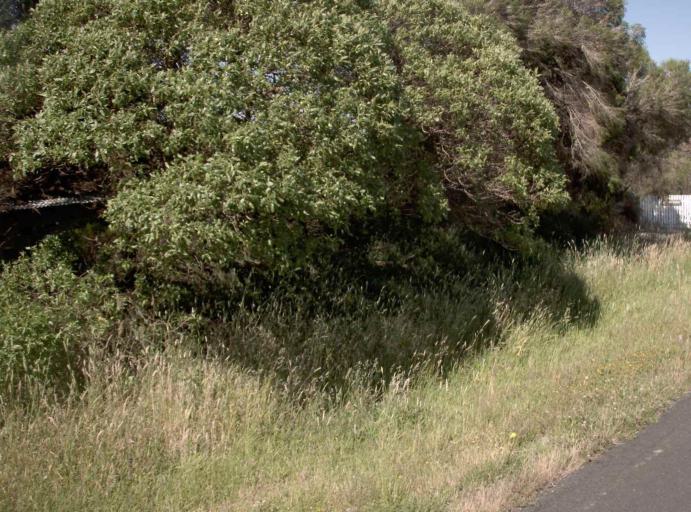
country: AU
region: Victoria
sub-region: Latrobe
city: Traralgon
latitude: -38.6239
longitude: 146.6442
